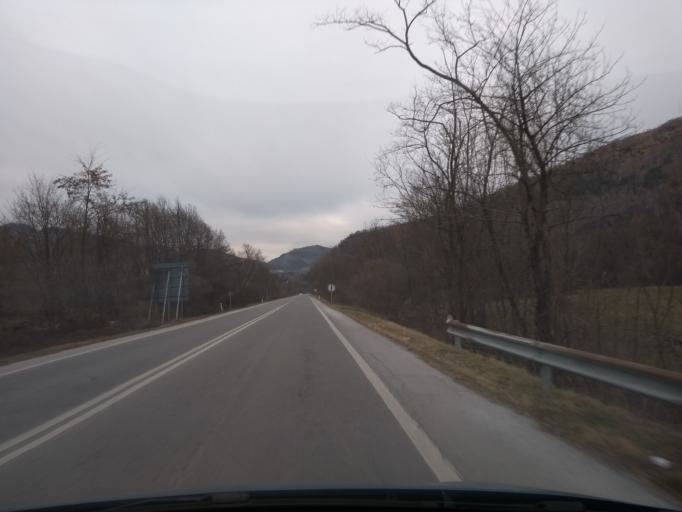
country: IT
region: Piedmont
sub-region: Provincia di Torino
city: Germagnano
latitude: 45.2591
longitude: 7.4708
